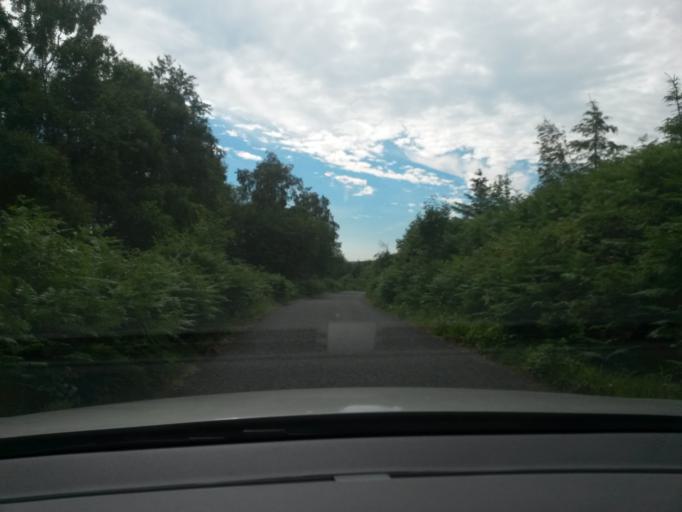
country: IE
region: Leinster
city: Ballinteer
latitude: 53.1854
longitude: -6.2840
